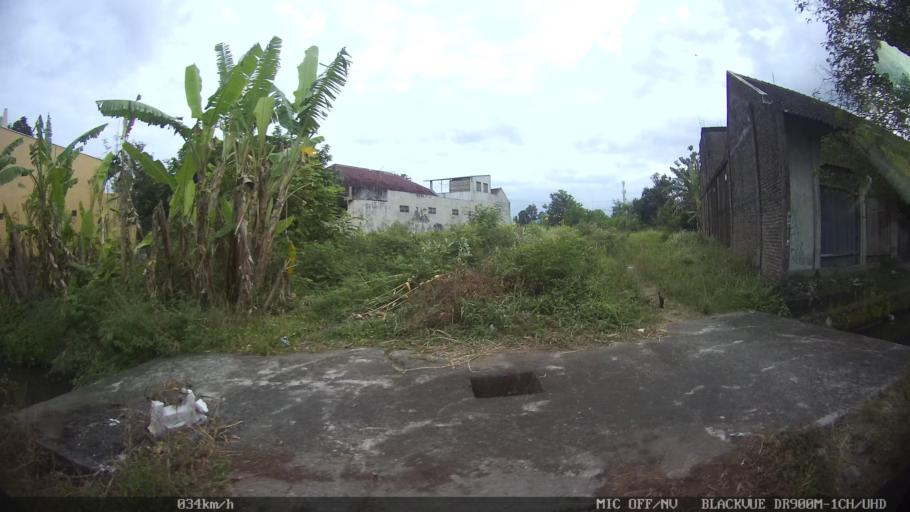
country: ID
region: Daerah Istimewa Yogyakarta
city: Sewon
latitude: -7.8363
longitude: 110.4167
